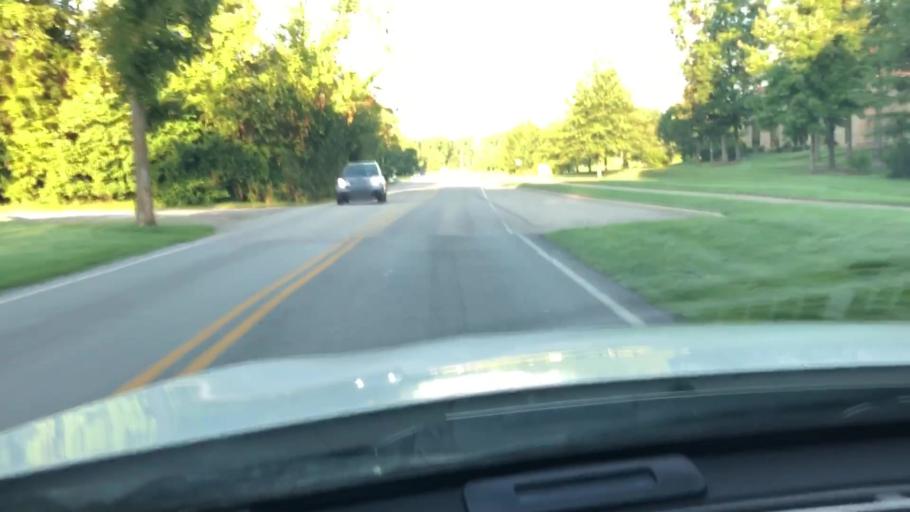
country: US
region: Kentucky
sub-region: Jefferson County
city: Middletown
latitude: 38.2175
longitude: -85.5271
